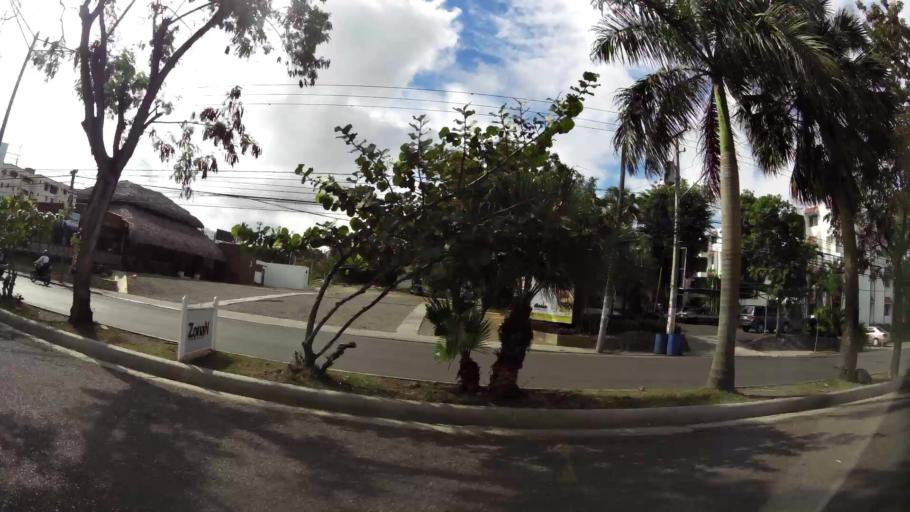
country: DO
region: Santiago
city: Santiago de los Caballeros
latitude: 19.4607
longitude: -70.6831
